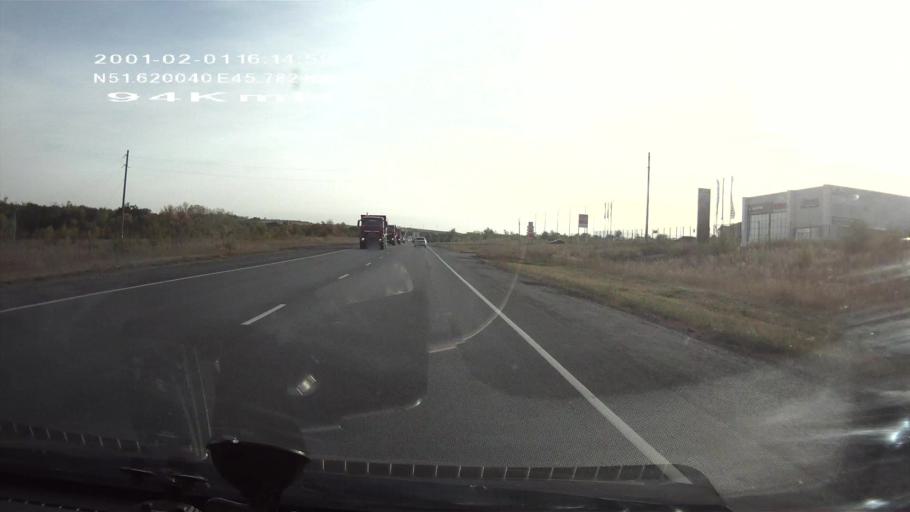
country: RU
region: Saratov
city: Sokolovyy
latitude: 51.6198
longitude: 45.7820
